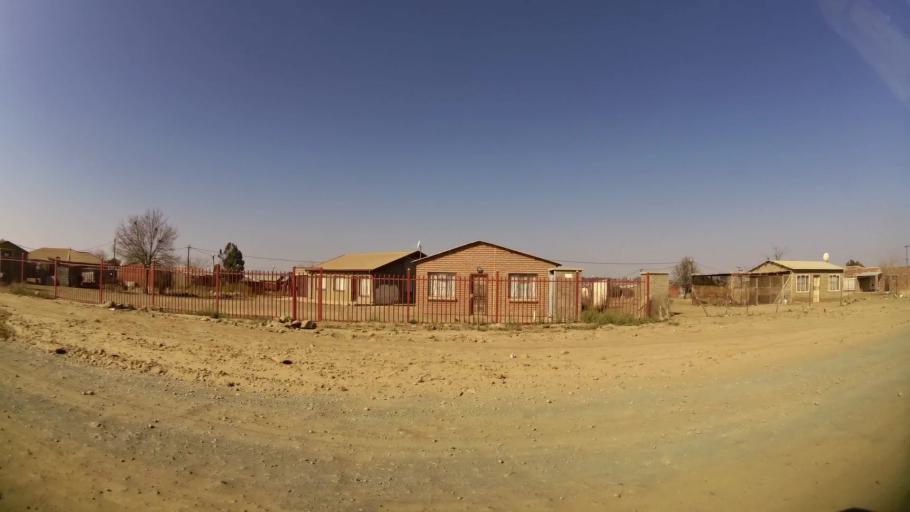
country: ZA
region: Orange Free State
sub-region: Mangaung Metropolitan Municipality
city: Bloemfontein
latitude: -29.1945
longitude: 26.2778
